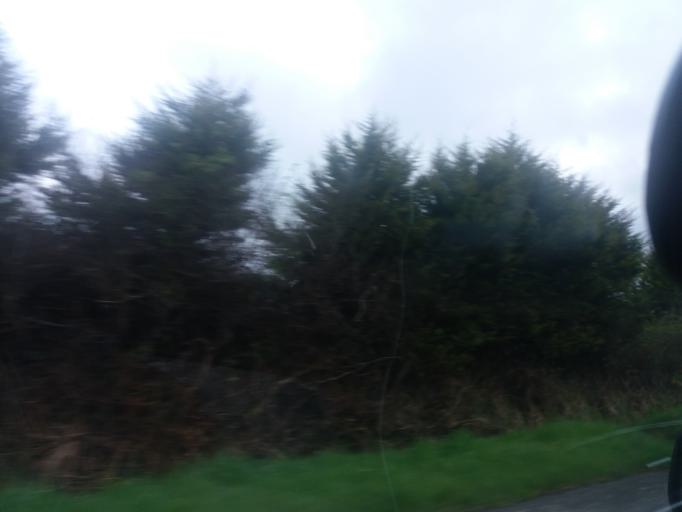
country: IE
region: Munster
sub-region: County Limerick
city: Abbeyfeale
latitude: 52.3898
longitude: -9.1950
